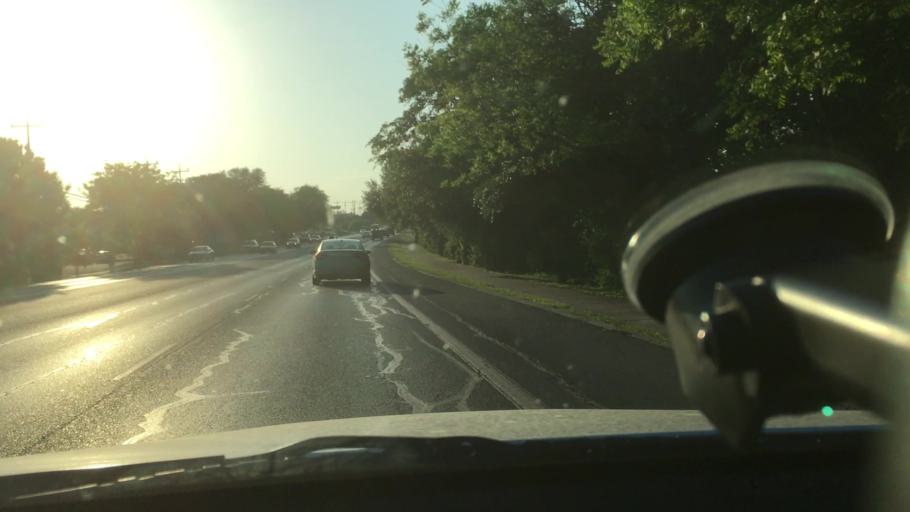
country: US
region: Texas
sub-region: Bexar County
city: Universal City
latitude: 29.5542
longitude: -98.3116
